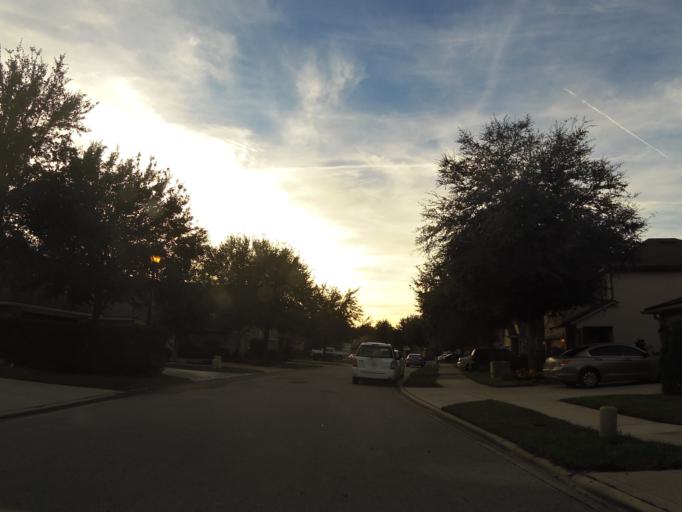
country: US
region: Florida
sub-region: Saint Johns County
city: Fruit Cove
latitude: 30.1605
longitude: -81.5488
